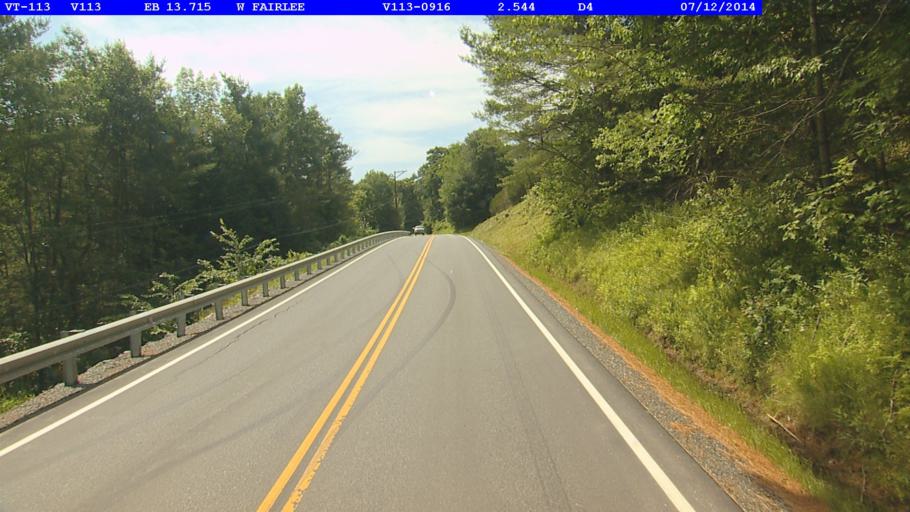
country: US
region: New Hampshire
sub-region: Grafton County
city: Orford
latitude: 43.9011
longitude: -72.2634
